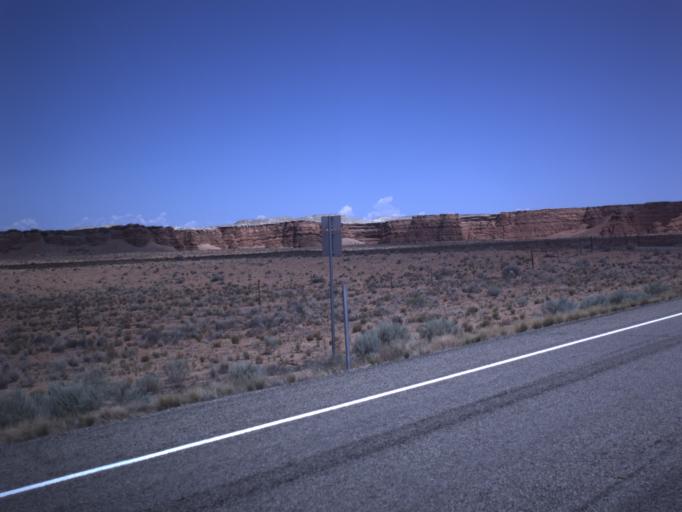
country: US
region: Utah
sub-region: Emery County
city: Ferron
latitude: 38.4292
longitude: -110.6917
